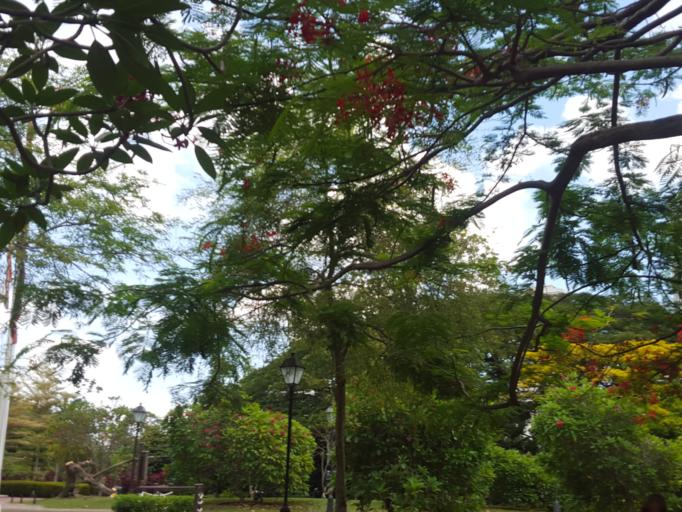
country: SG
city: Singapore
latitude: 1.2916
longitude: 103.8474
